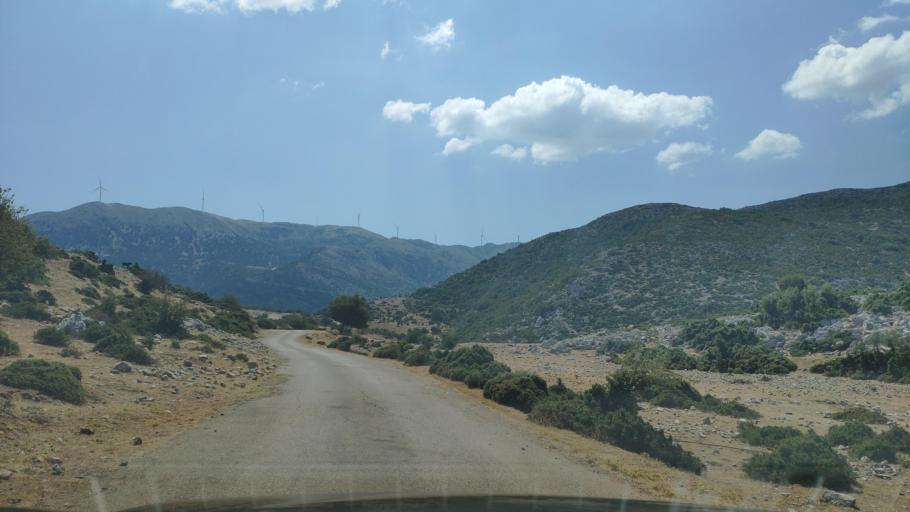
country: GR
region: West Greece
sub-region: Nomos Aitolias kai Akarnanias
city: Monastirakion
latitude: 38.7990
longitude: 20.9496
